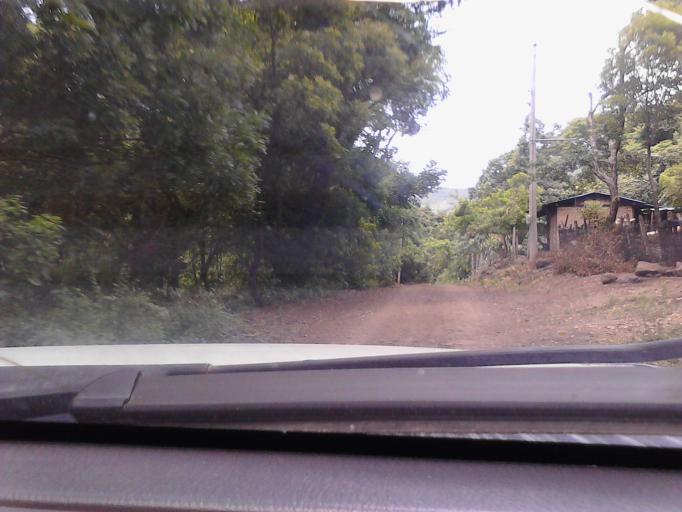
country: NI
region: Matagalpa
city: Terrabona
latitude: 12.7087
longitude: -85.9449
